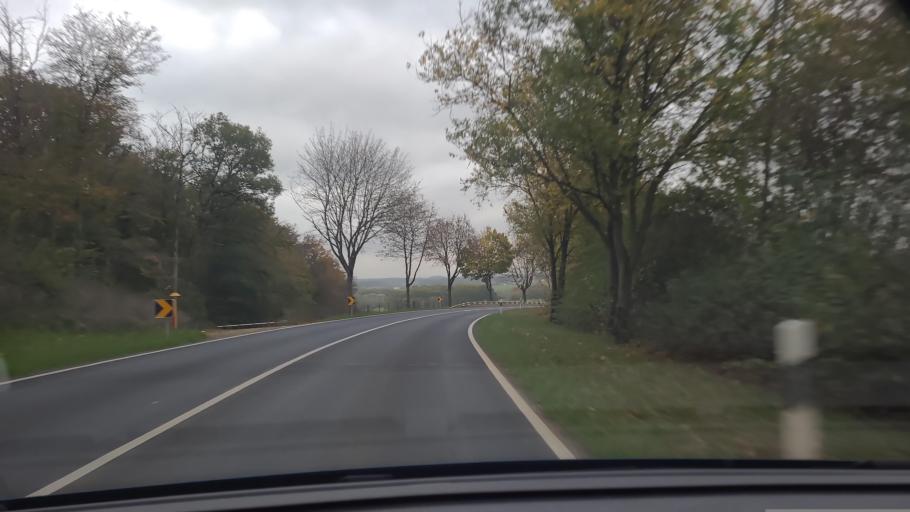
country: LU
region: Luxembourg
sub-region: Canton de Capellen
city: Garnich
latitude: 49.6258
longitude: 5.9525
